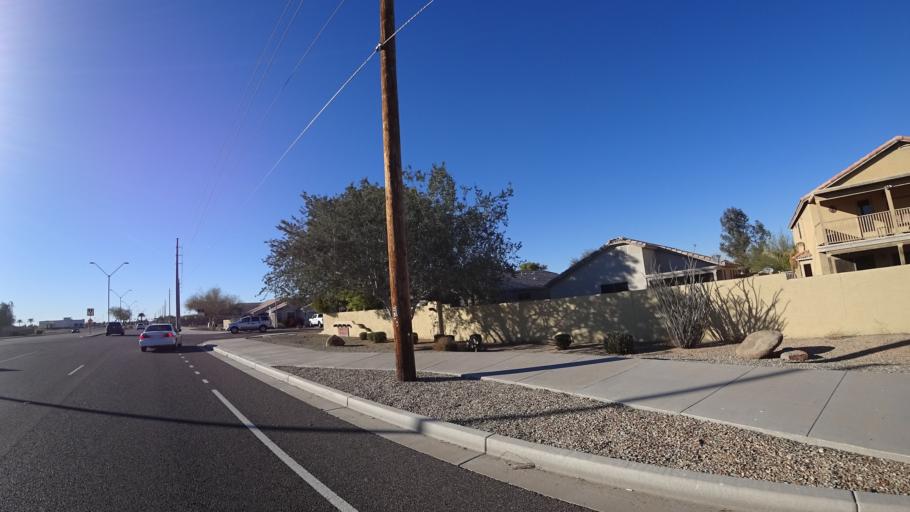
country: US
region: Arizona
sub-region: Maricopa County
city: Goodyear
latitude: 33.4501
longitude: -112.3872
